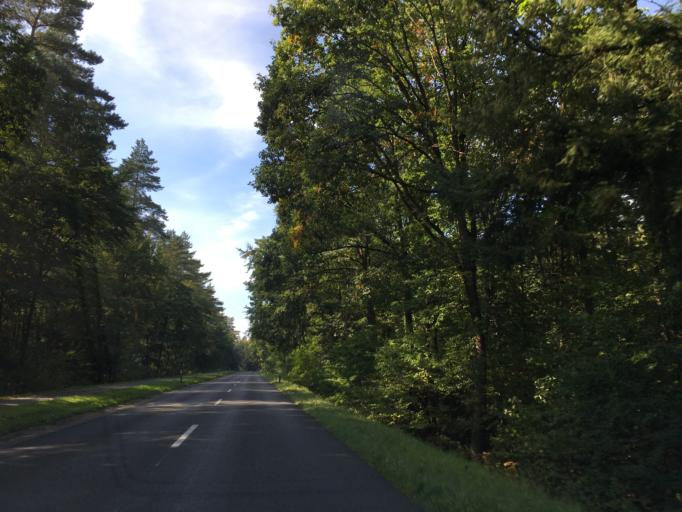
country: DE
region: Lower Saxony
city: Adendorf
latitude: 53.2907
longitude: 10.4728
